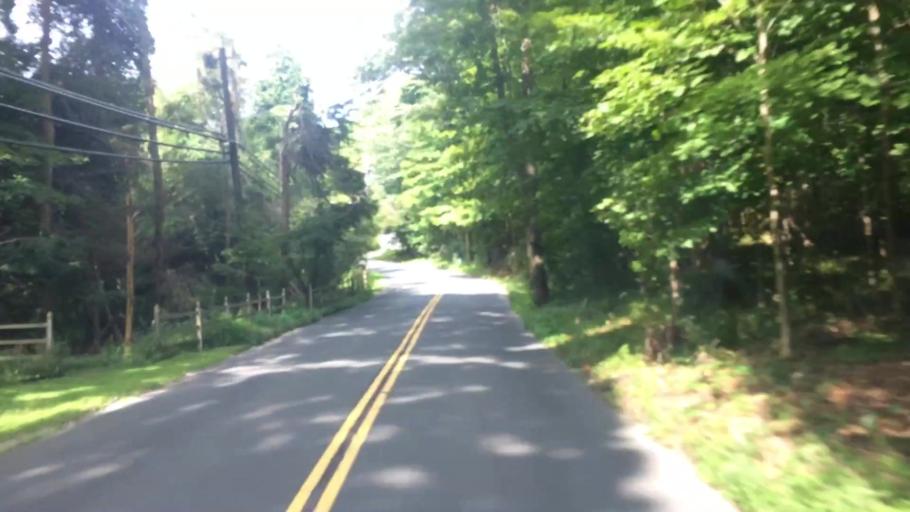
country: US
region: Connecticut
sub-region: Fairfield County
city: Danbury
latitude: 41.4075
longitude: -73.4806
